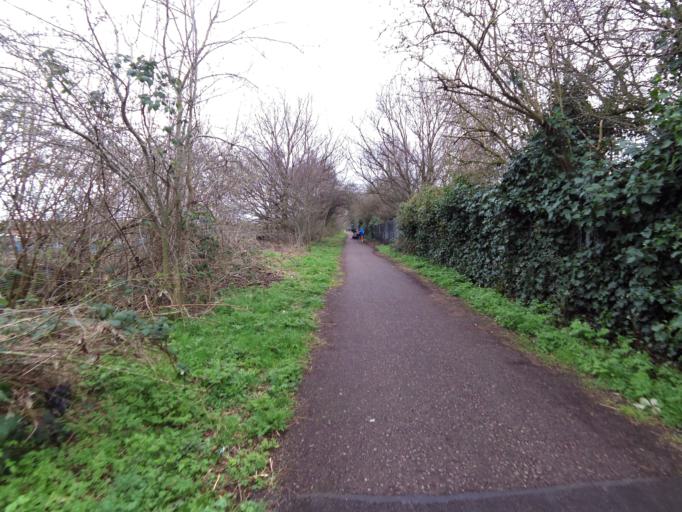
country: GB
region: England
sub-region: Doncaster
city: Bentley
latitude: 53.5418
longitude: -1.1573
